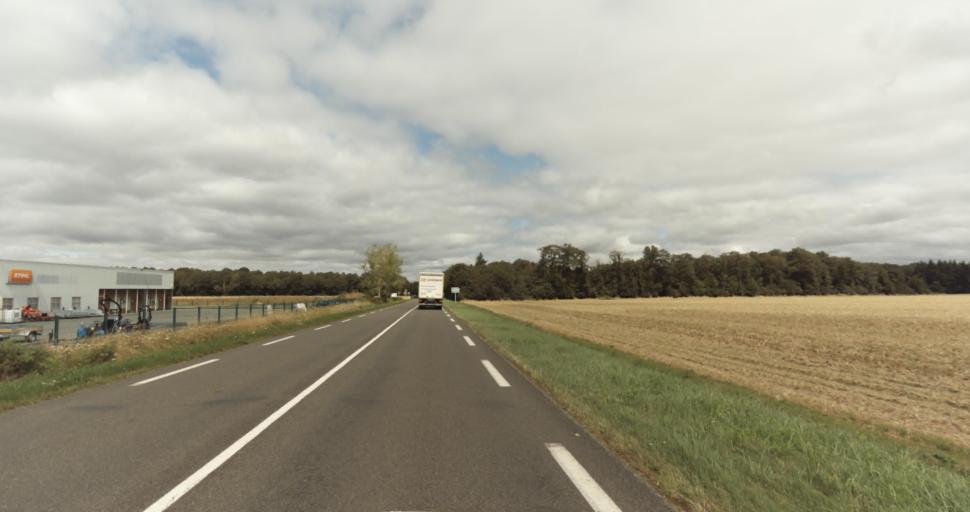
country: FR
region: Haute-Normandie
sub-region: Departement de l'Eure
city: Evreux
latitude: 48.9595
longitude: 1.1613
